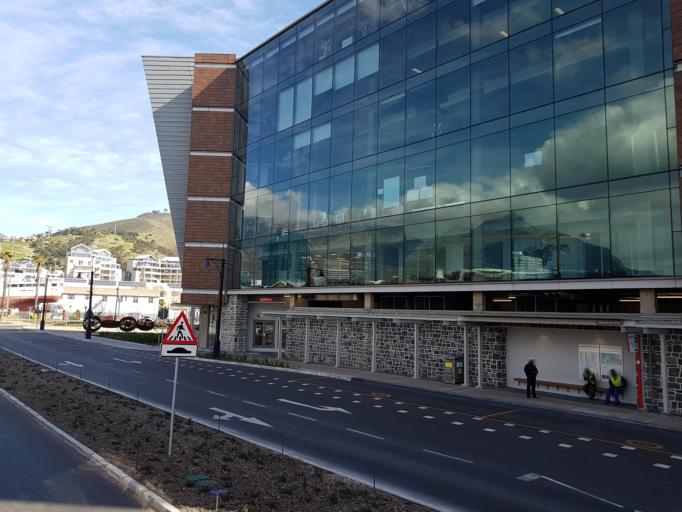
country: ZA
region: Western Cape
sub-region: City of Cape Town
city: Cape Town
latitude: -33.9094
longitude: 18.4237
